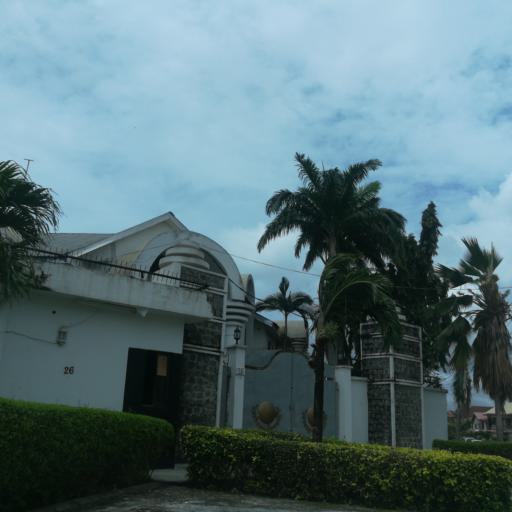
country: NG
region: Lagos
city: Ikoyi
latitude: 6.4430
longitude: 3.4624
